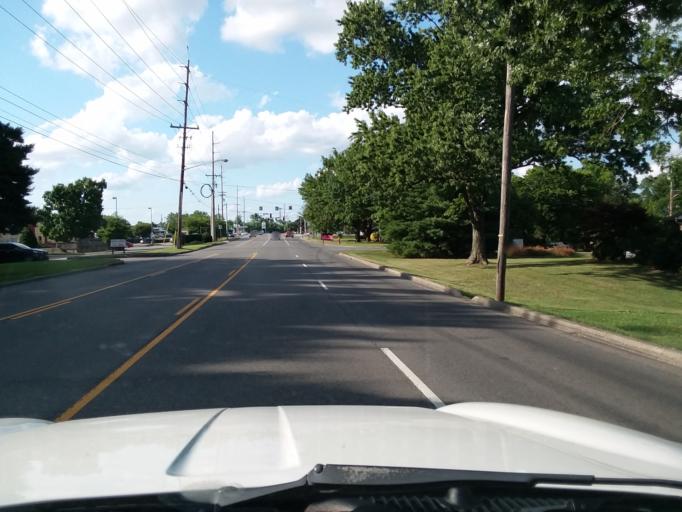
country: US
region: Tennessee
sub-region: Davidson County
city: Oak Hill
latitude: 36.0790
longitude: -86.7586
